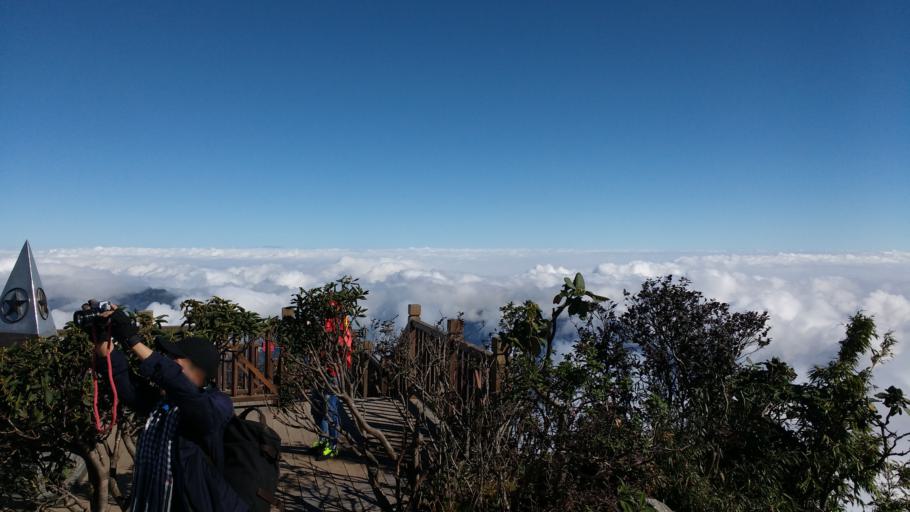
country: VN
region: Lao Cai
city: Sa Pa
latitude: 22.3032
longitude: 103.7753
